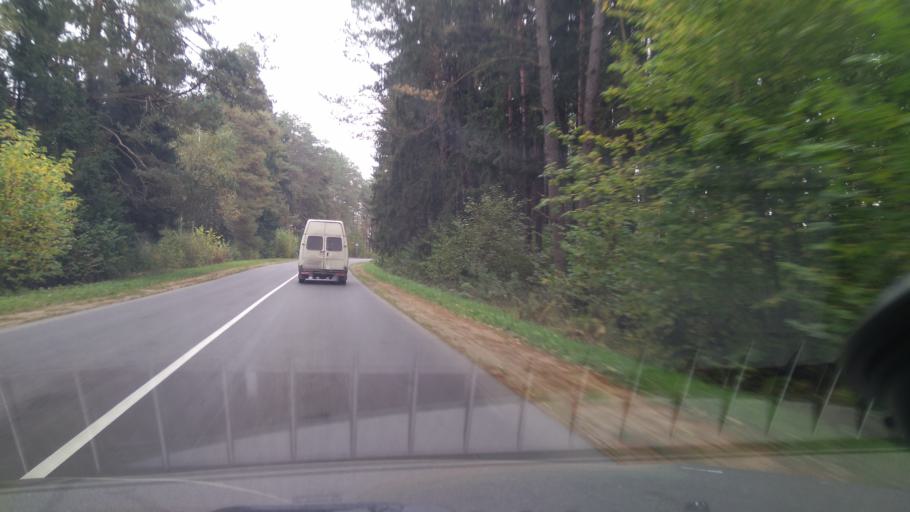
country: BY
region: Minsk
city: Rudzyensk
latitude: 53.6131
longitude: 27.7897
